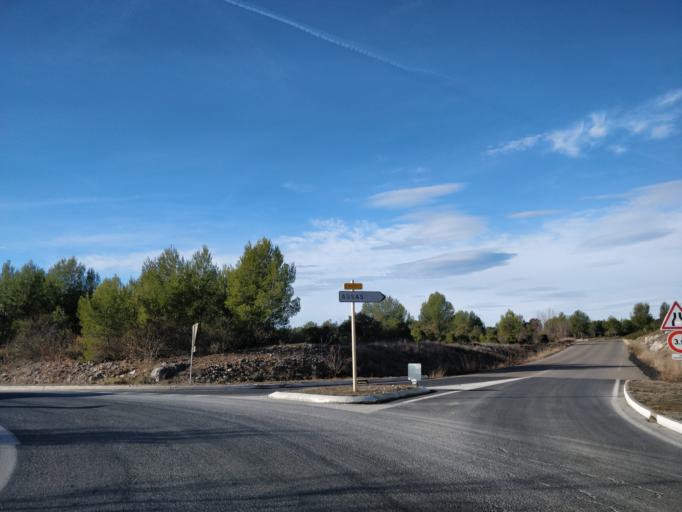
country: FR
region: Languedoc-Roussillon
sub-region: Departement de l'Herault
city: Teyran
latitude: 43.7053
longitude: 3.9371
